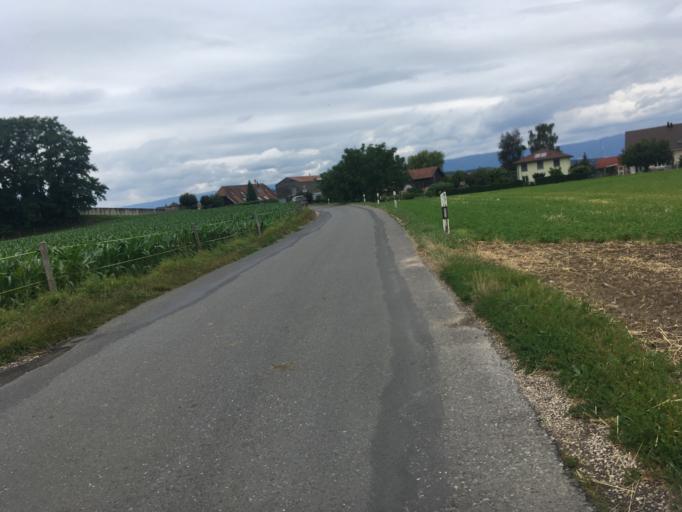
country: CH
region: Fribourg
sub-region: See District
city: Gurwolf
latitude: 46.9069
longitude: 7.0832
